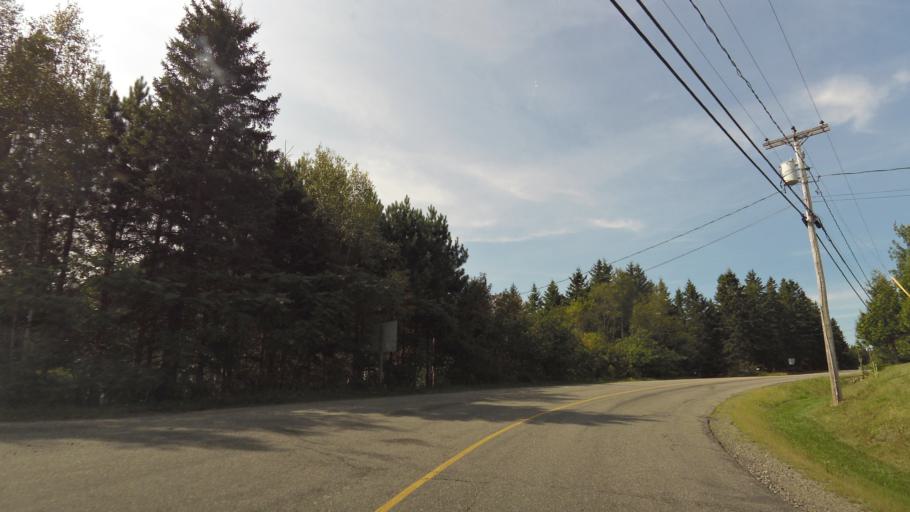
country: CA
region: New Brunswick
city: Hampton
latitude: 45.5369
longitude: -65.8640
